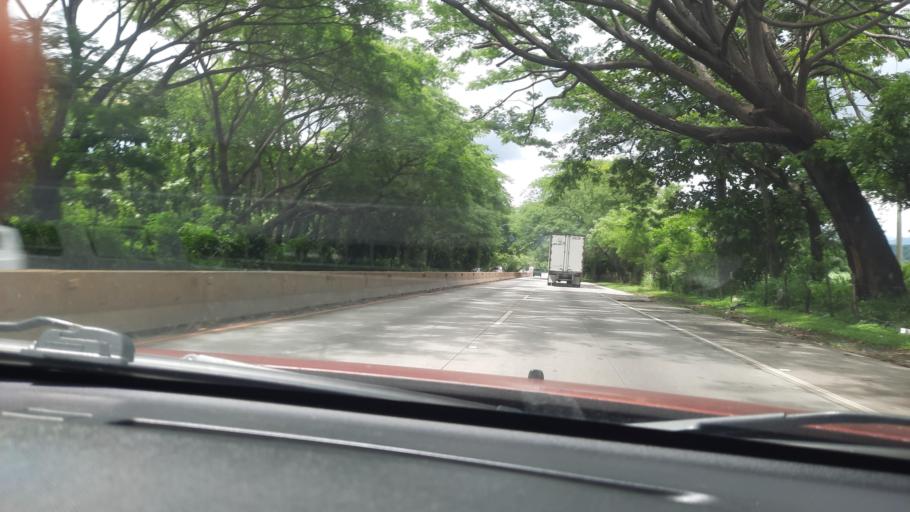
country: SV
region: Sonsonate
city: Sonzacate
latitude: 13.7253
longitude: -89.7039
